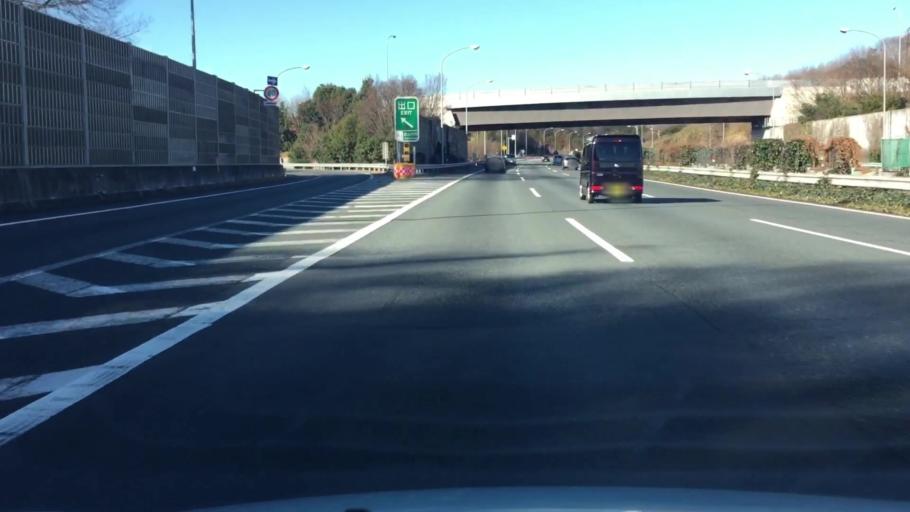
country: JP
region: Saitama
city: Ogawa
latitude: 36.0675
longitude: 139.3144
